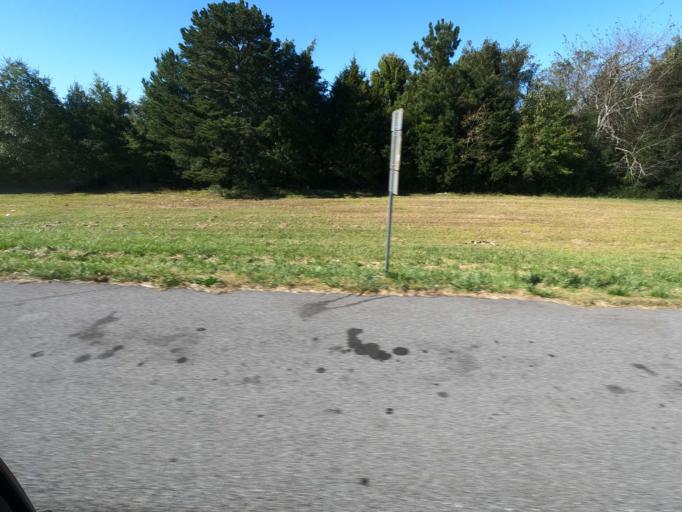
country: US
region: Alabama
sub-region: Limestone County
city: Ardmore
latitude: 34.9736
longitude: -86.8838
